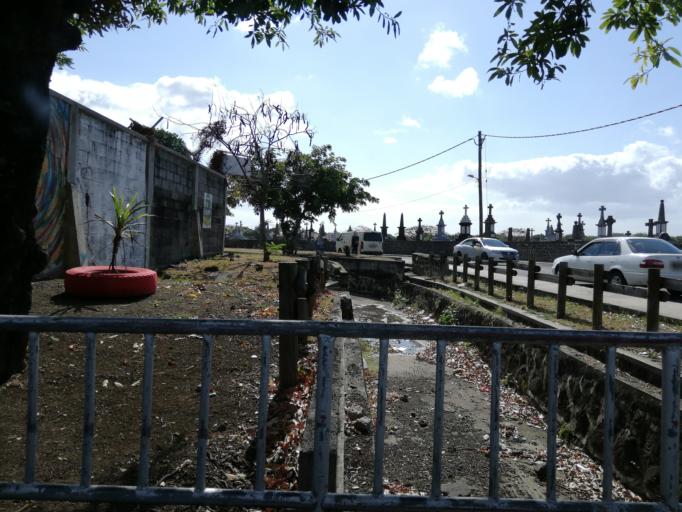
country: MU
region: Port Louis
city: Port Louis
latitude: -20.1633
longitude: 57.4872
